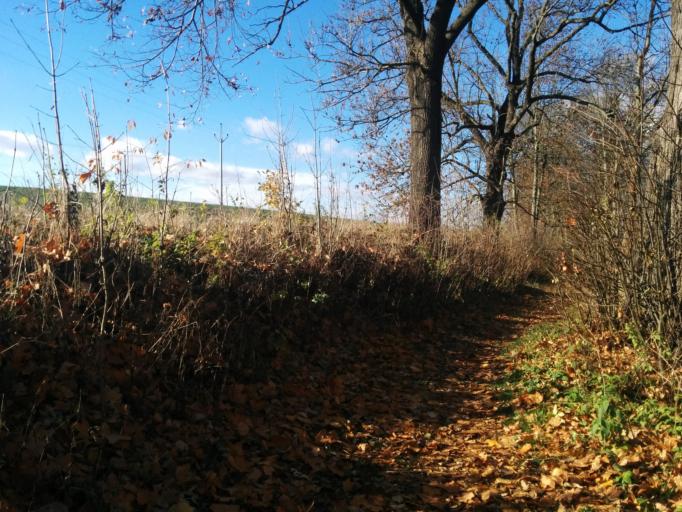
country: CZ
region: Vysocina
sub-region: Okres Jihlava
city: Jihlava
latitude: 49.4092
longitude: 15.5579
